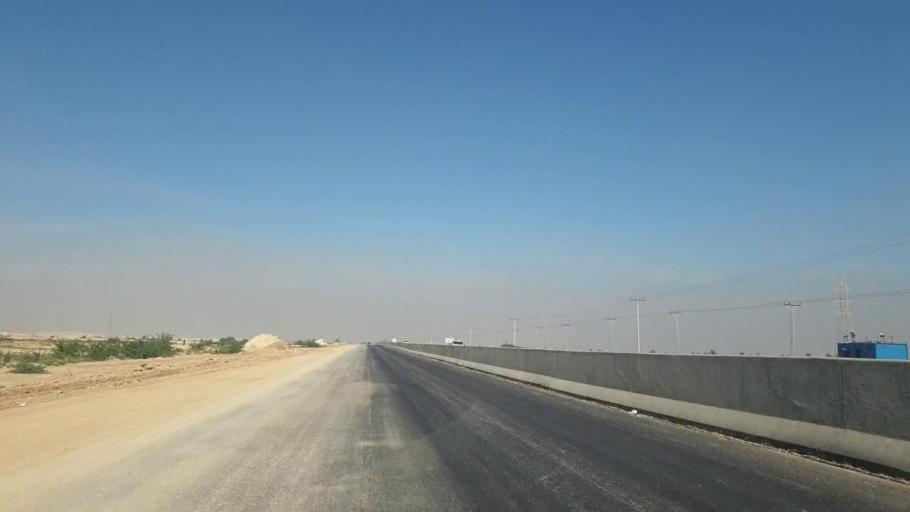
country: PK
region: Sindh
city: Jamshoro
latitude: 25.5140
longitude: 68.2738
